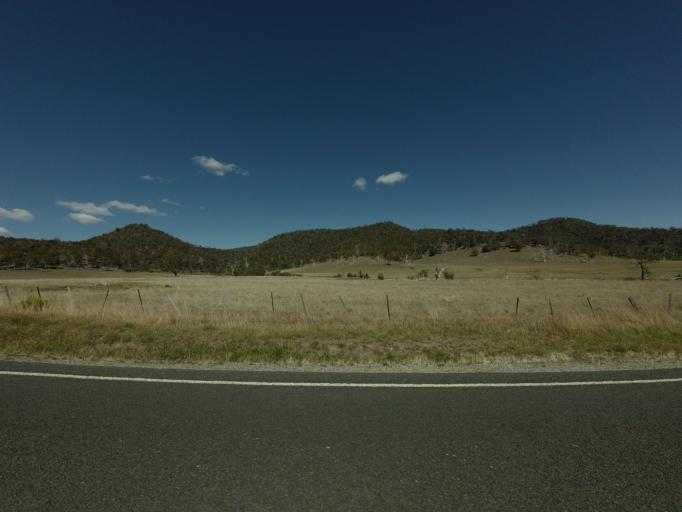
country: AU
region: Tasmania
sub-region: Break O'Day
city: St Helens
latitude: -41.6904
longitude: 147.8766
